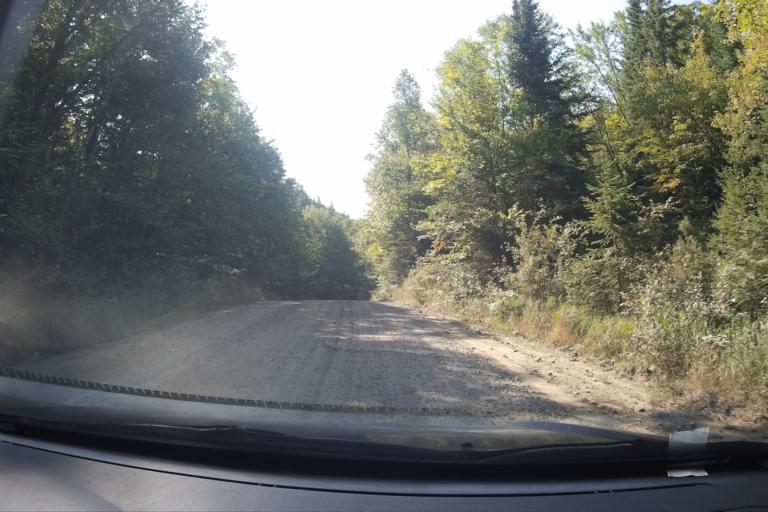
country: CA
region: Ontario
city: Huntsville
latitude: 45.5475
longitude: -78.6955
